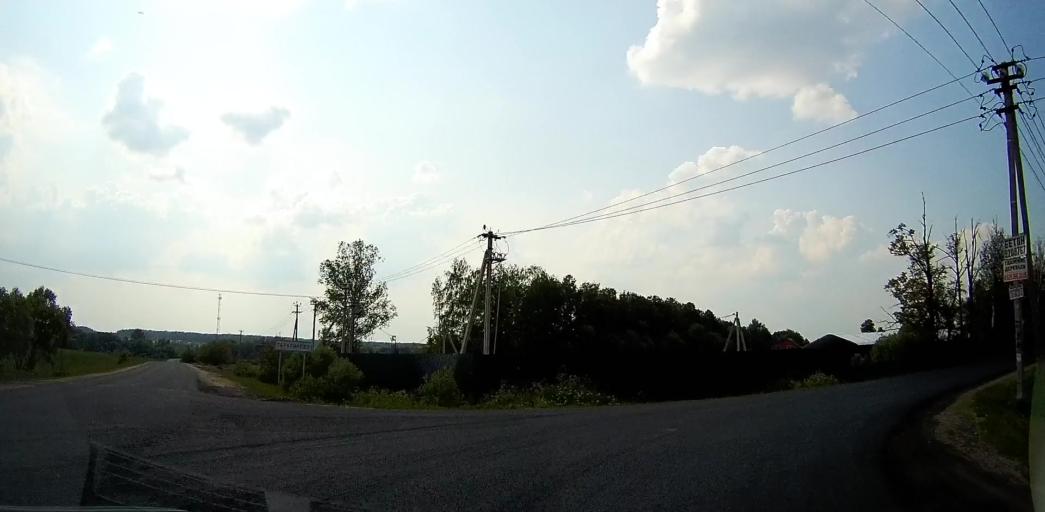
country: RU
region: Moskovskaya
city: Il'inskoye
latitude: 55.2114
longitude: 37.9473
